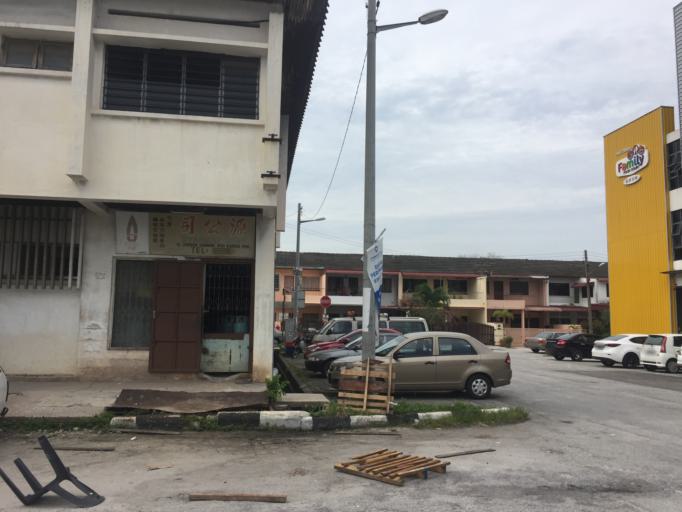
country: MY
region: Perak
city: Ipoh
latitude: 4.6109
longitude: 101.1103
